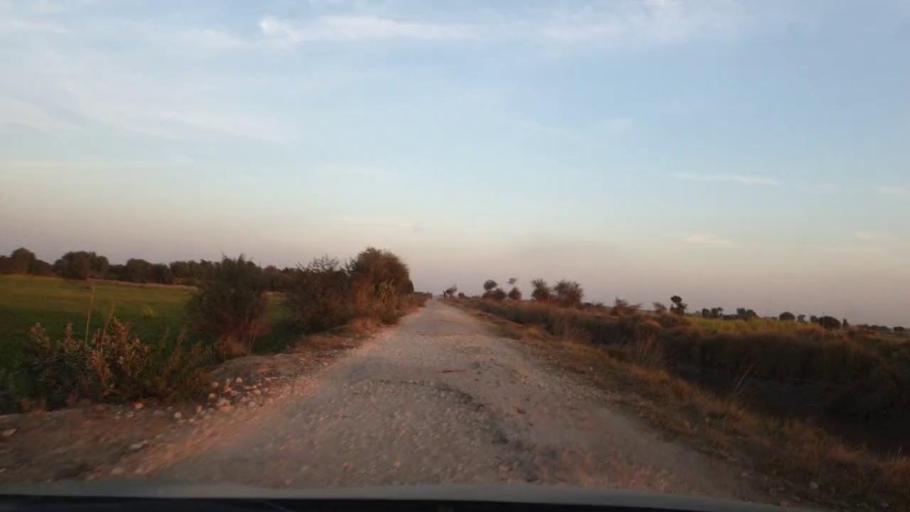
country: PK
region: Sindh
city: Tando Allahyar
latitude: 25.5855
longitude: 68.7200
